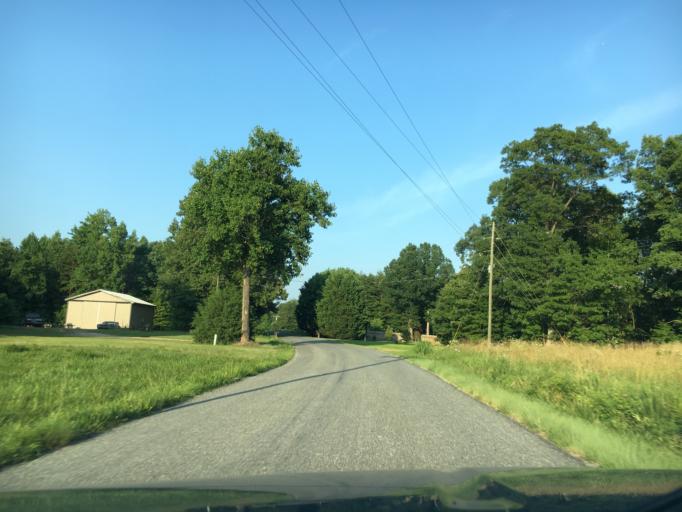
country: US
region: Virginia
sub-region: Pittsylvania County
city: Gretna
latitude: 36.8419
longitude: -79.1909
